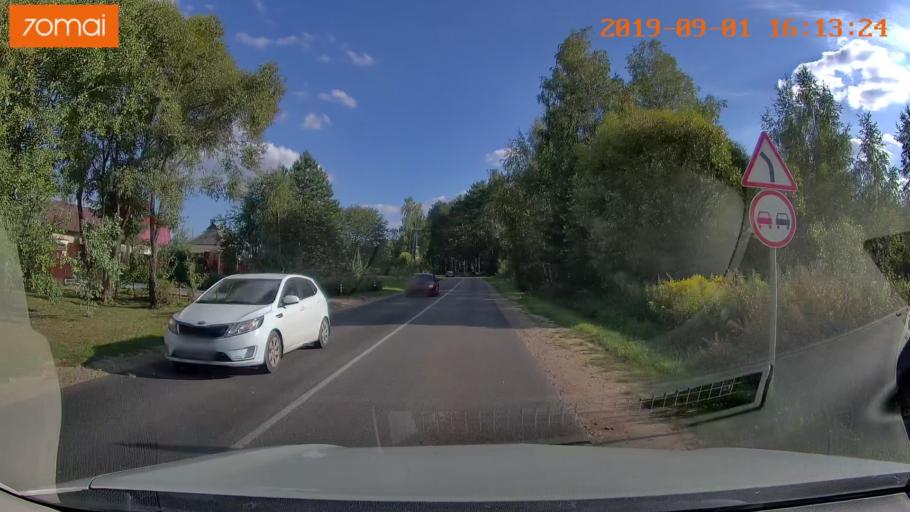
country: RU
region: Kaluga
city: Maloyaroslavets
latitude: 54.9413
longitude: 36.4595
